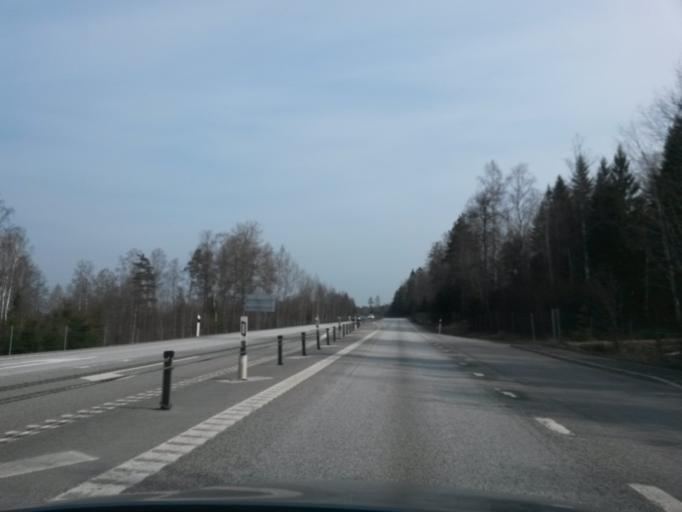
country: SE
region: Vaestra Goetaland
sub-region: Toreboda Kommun
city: Toereboda
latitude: 58.7775
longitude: 14.0040
